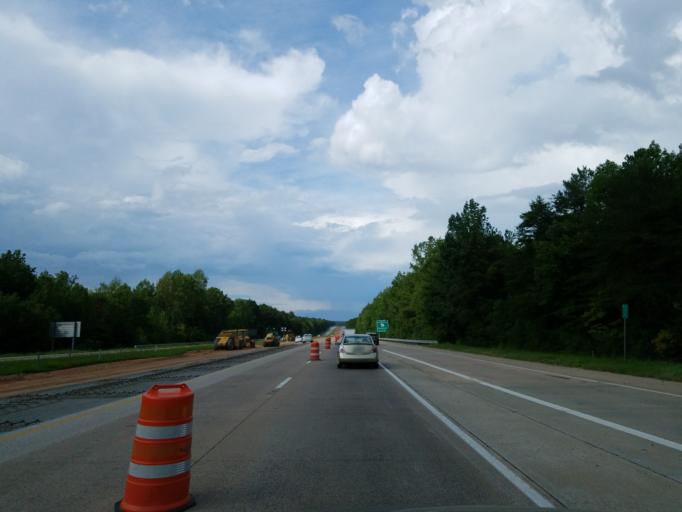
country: US
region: Georgia
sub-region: Forsyth County
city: Cumming
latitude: 34.2334
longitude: -84.1000
